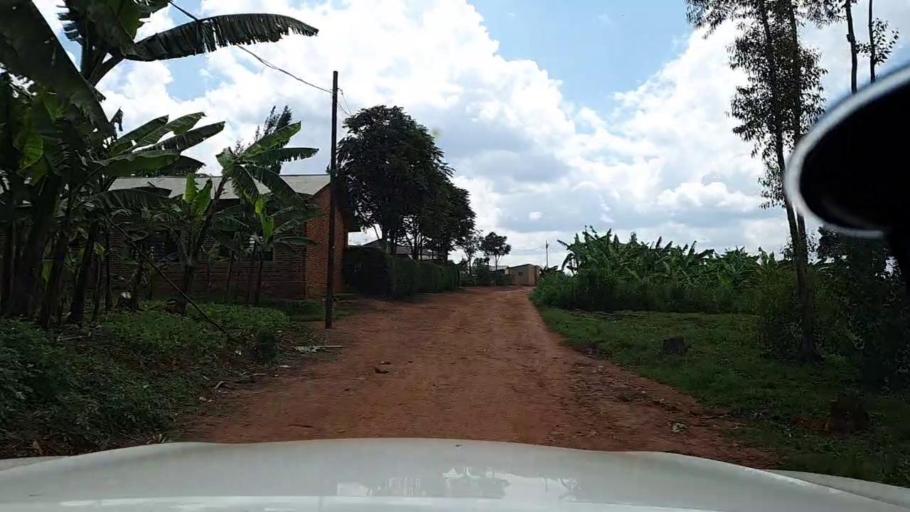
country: RW
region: Southern Province
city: Gitarama
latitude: -1.8373
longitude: 29.8325
